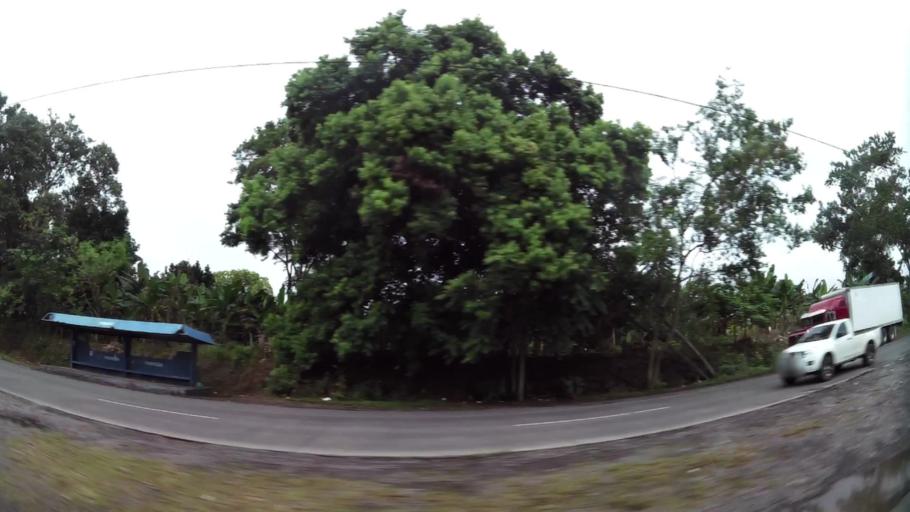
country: PA
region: Chiriqui
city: La Concepcion
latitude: 8.5080
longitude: -82.6122
